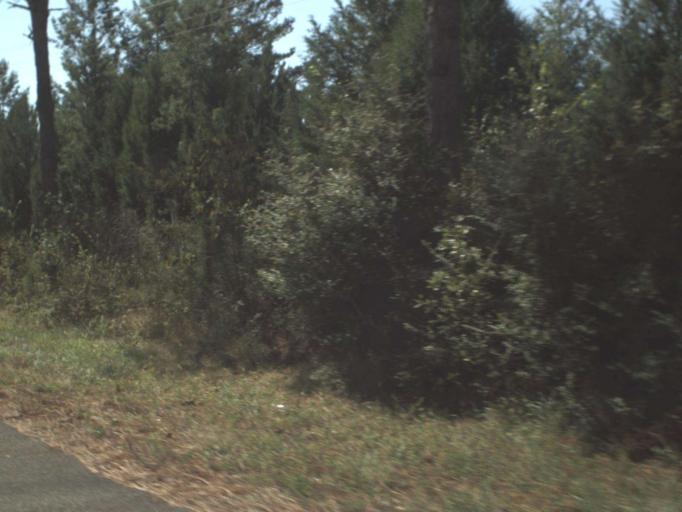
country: US
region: Florida
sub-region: Walton County
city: DeFuniak Springs
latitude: 30.9158
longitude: -86.1347
